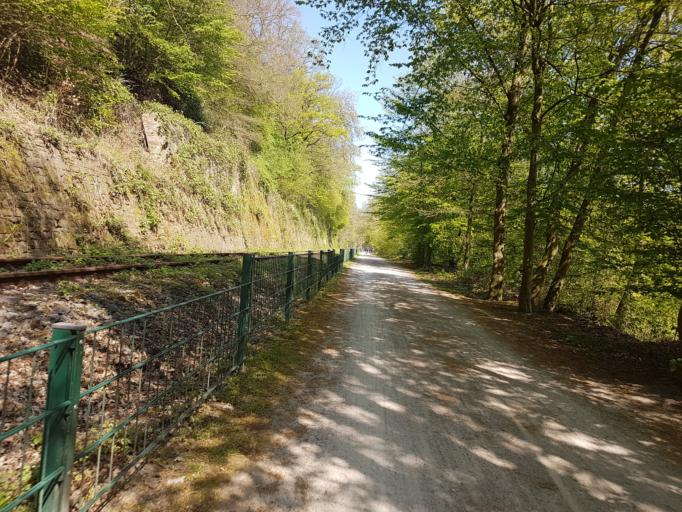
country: DE
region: North Rhine-Westphalia
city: Witten
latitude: 51.4154
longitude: 7.3468
